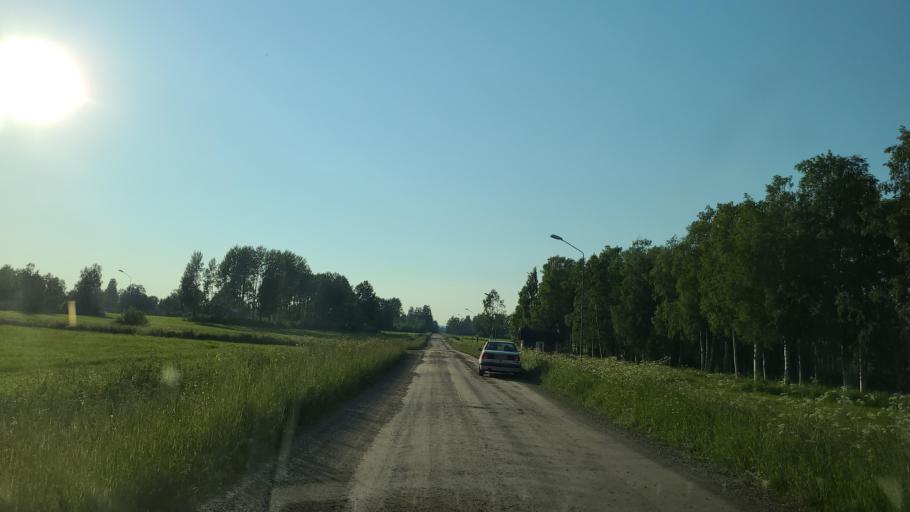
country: SE
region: Vaesterbotten
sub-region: Skelleftea Kommun
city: Burea
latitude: 64.3976
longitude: 21.3775
